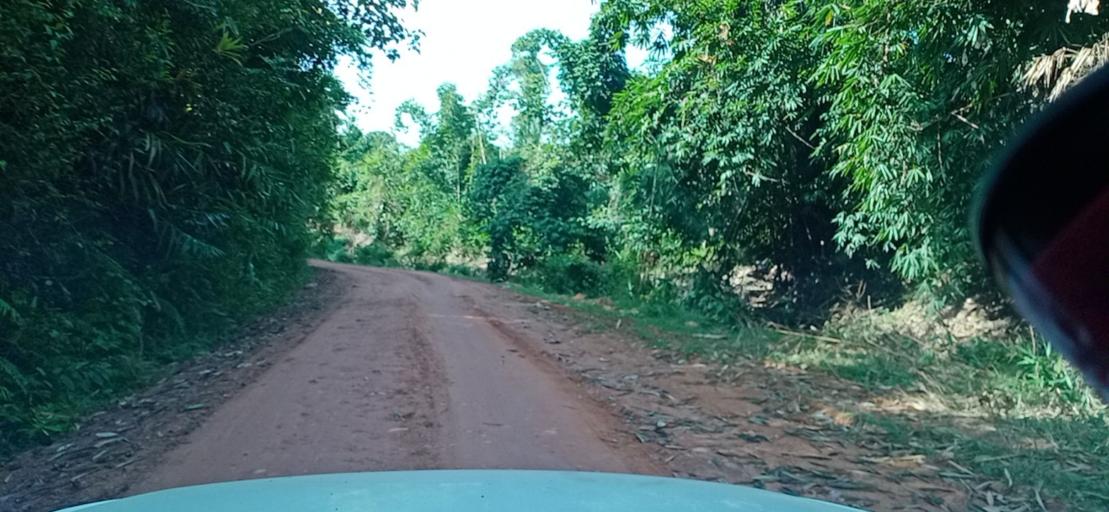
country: TH
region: Changwat Bueng Kan
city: Pak Khat
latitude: 18.6645
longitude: 103.1979
